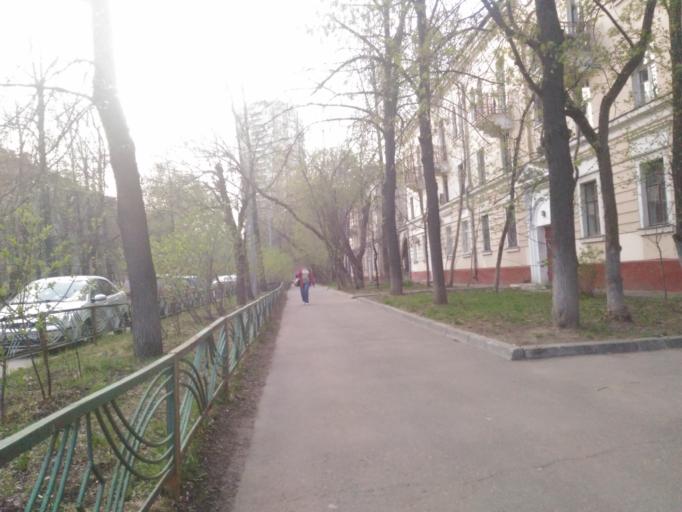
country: RU
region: Moskovskaya
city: Khoroshevo-Mnevniki
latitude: 55.7940
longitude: 37.4896
